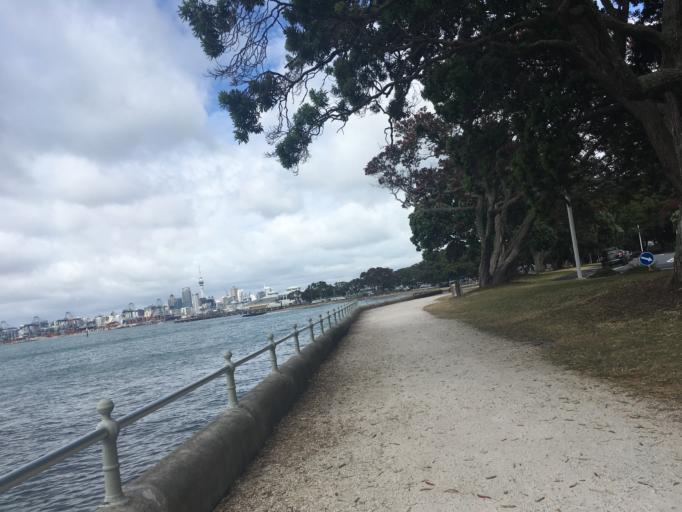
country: NZ
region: Auckland
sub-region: Auckland
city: Auckland
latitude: -36.8317
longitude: 174.8006
